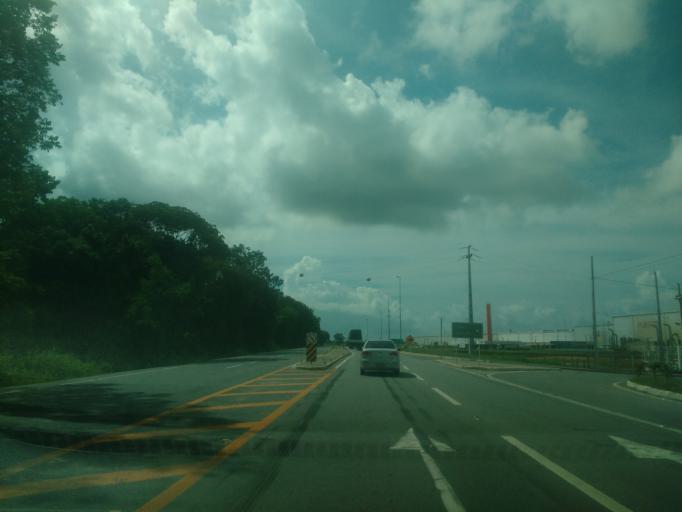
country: BR
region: Alagoas
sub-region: Marechal Deodoro
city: Marechal Deodoro
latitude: -9.6830
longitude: -35.8287
